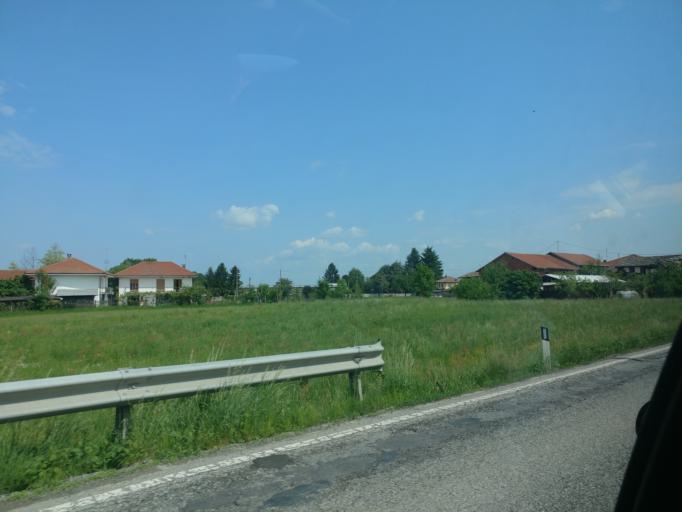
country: IT
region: Piedmont
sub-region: Provincia di Torino
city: Cavour
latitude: 44.7474
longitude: 7.4091
